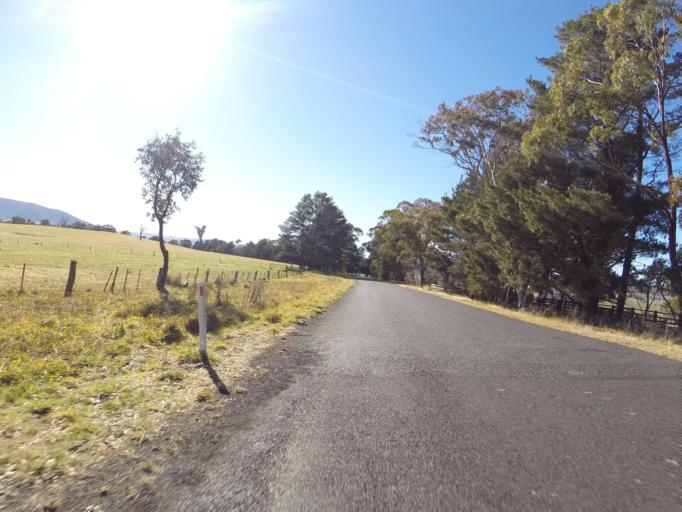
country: AU
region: New South Wales
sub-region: Oberon
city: Oberon
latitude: -33.5730
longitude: 149.8673
